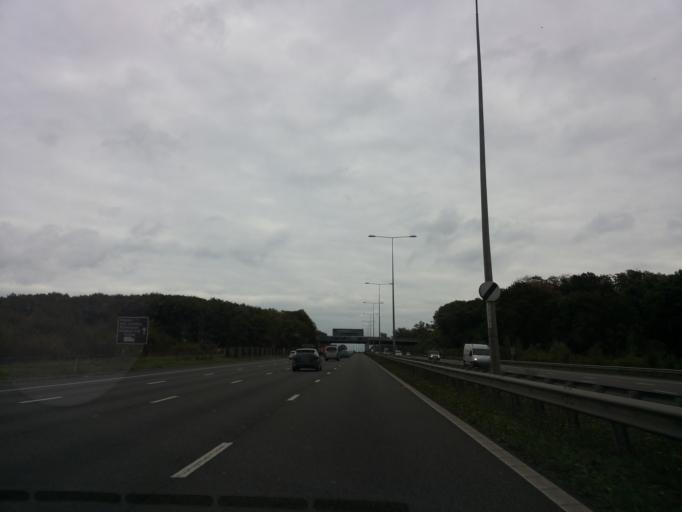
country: GB
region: England
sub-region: Kent
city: Gravesend
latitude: 51.4041
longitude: 0.4001
